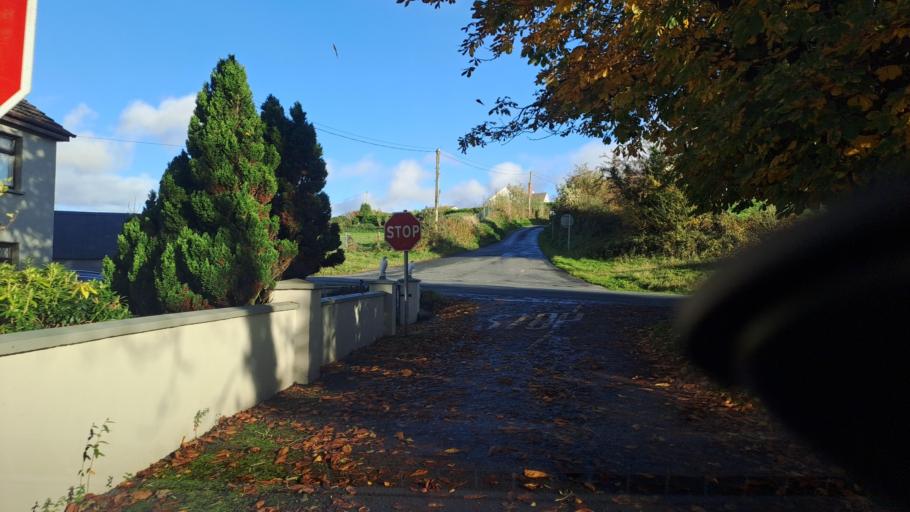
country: IE
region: Ulster
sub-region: An Cabhan
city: Bailieborough
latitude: 53.9214
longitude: -6.9491
